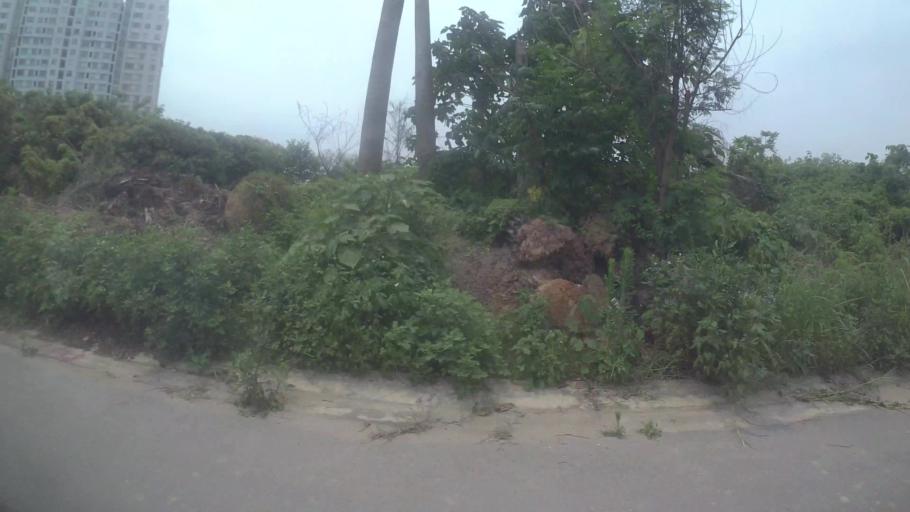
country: VN
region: Ha Noi
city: Cau Dien
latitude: 21.0278
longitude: 105.7419
